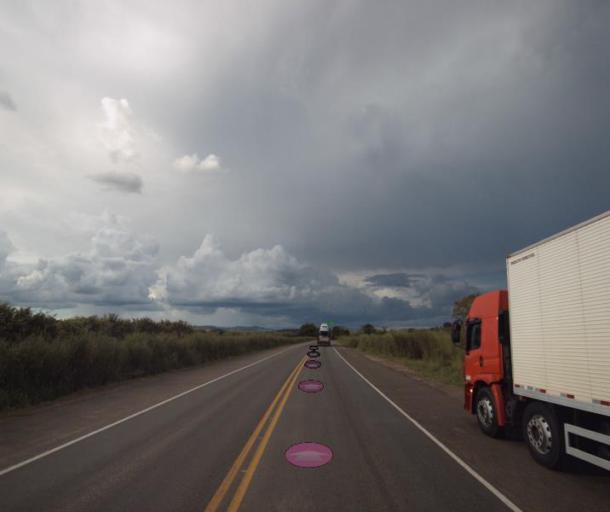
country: BR
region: Goias
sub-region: Ceres
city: Ceres
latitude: -15.2254
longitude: -49.5537
